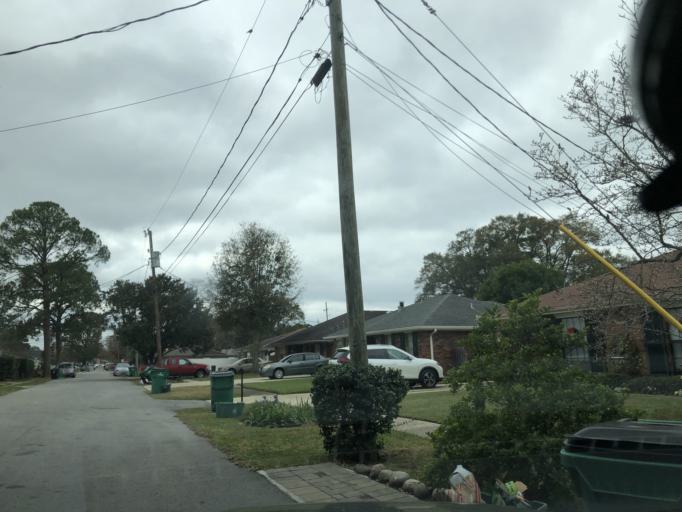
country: US
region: Louisiana
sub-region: Jefferson Parish
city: Metairie
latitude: 29.9900
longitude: -90.1530
